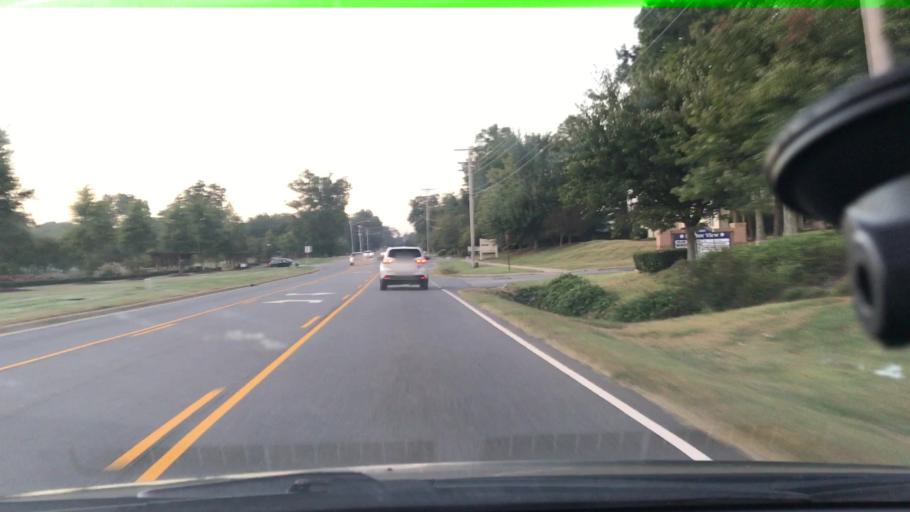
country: US
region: North Carolina
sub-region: Mecklenburg County
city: Cornelius
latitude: 35.4595
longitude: -80.8886
